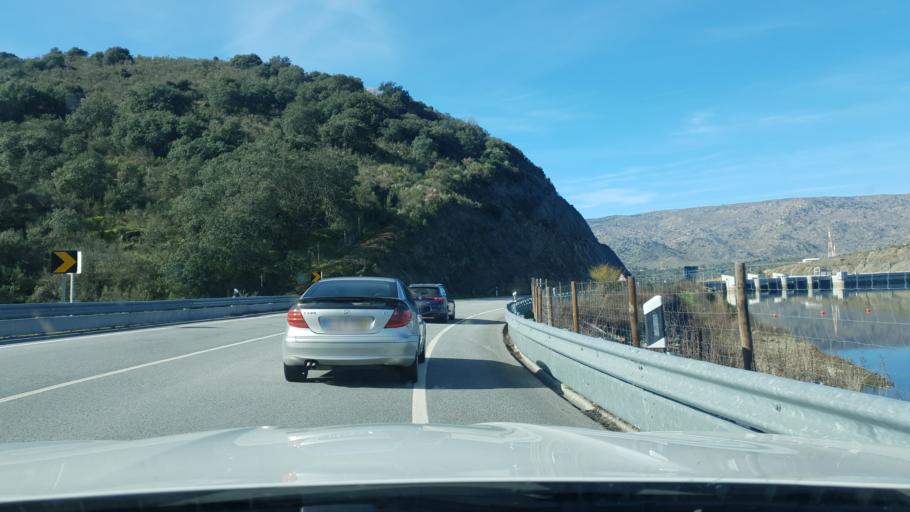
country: PT
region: Braganca
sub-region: Torre de Moncorvo
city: Torre de Moncorvo
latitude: 41.2011
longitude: -7.0874
